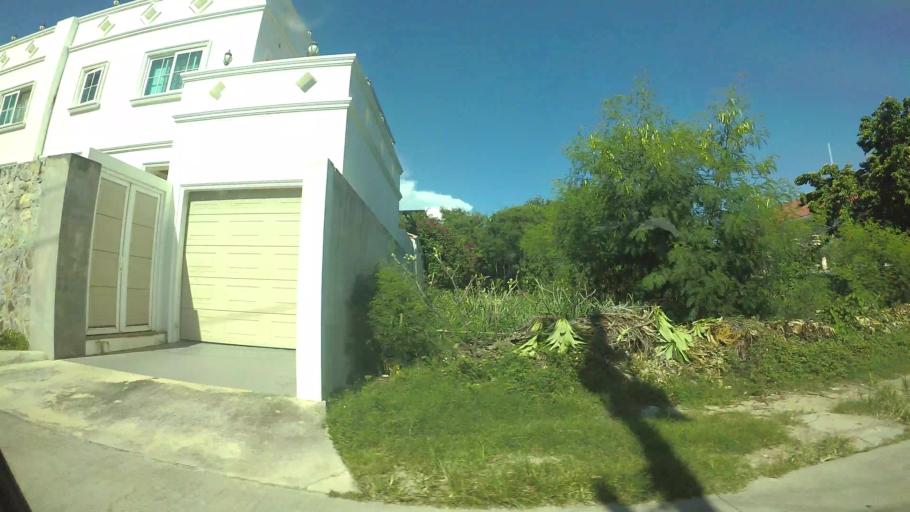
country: TH
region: Chon Buri
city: Phatthaya
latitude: 12.9121
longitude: 100.8593
